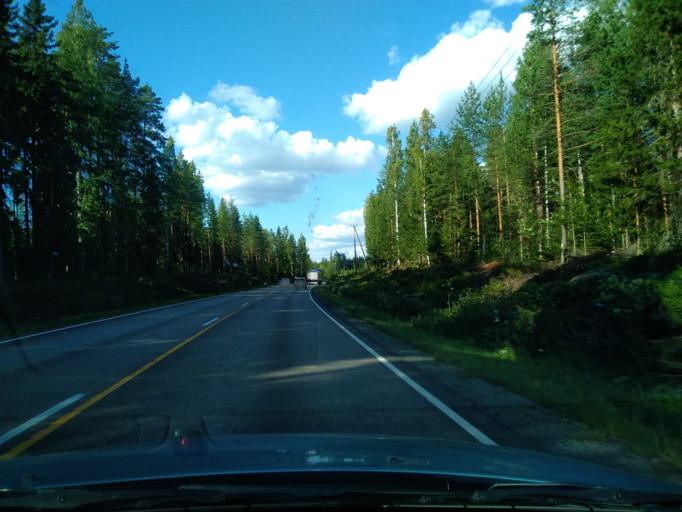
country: FI
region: Pirkanmaa
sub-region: Ylae-Pirkanmaa
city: Maenttae
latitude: 62.1091
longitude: 24.7388
